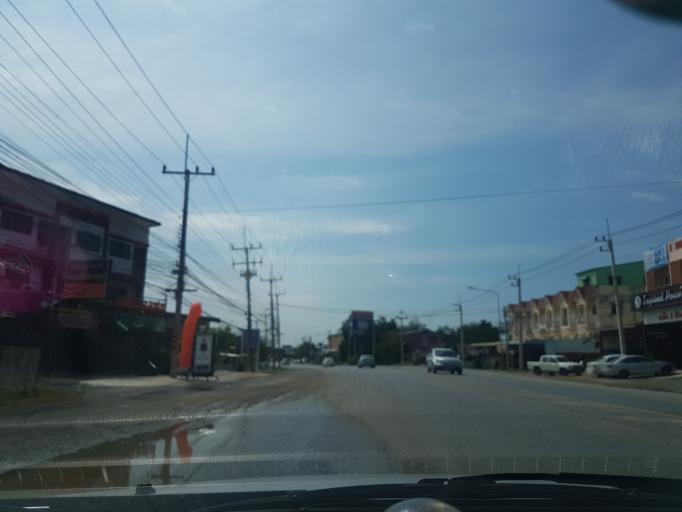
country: TH
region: Lop Buri
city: Lop Buri
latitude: 14.7914
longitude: 100.7039
